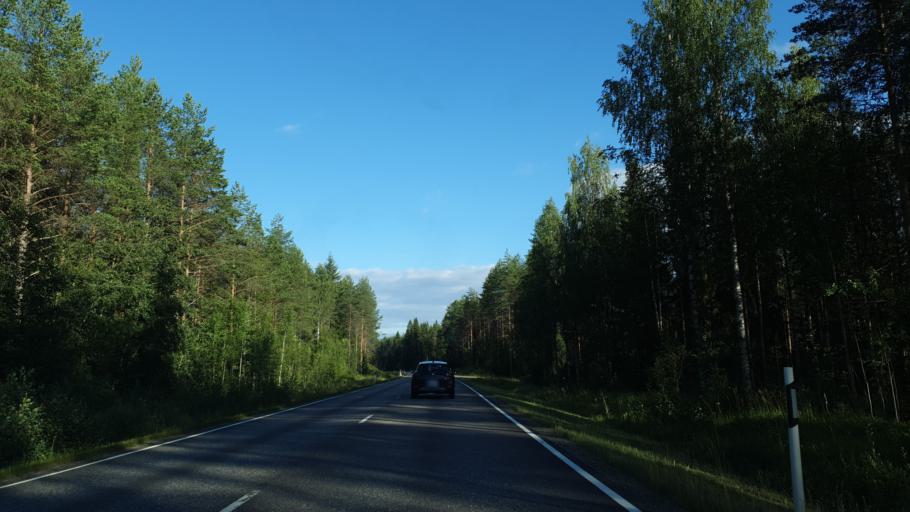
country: FI
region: North Karelia
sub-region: Joensuu
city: Outokumpu
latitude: 62.5234
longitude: 29.0006
